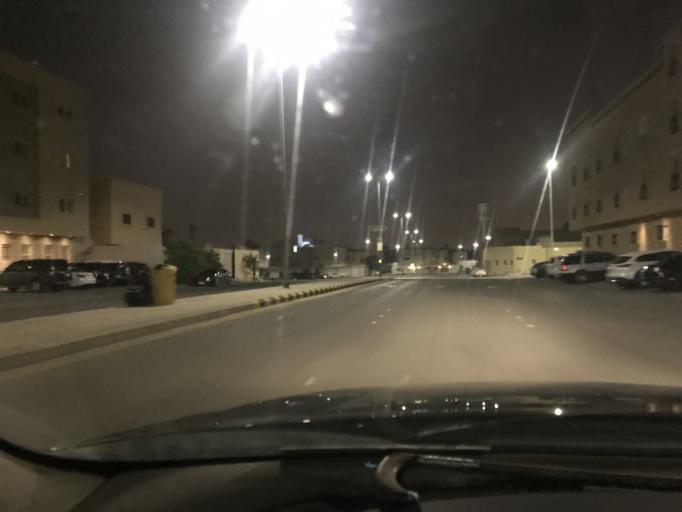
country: SA
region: Ar Riyad
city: Riyadh
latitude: 24.7263
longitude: 46.7907
